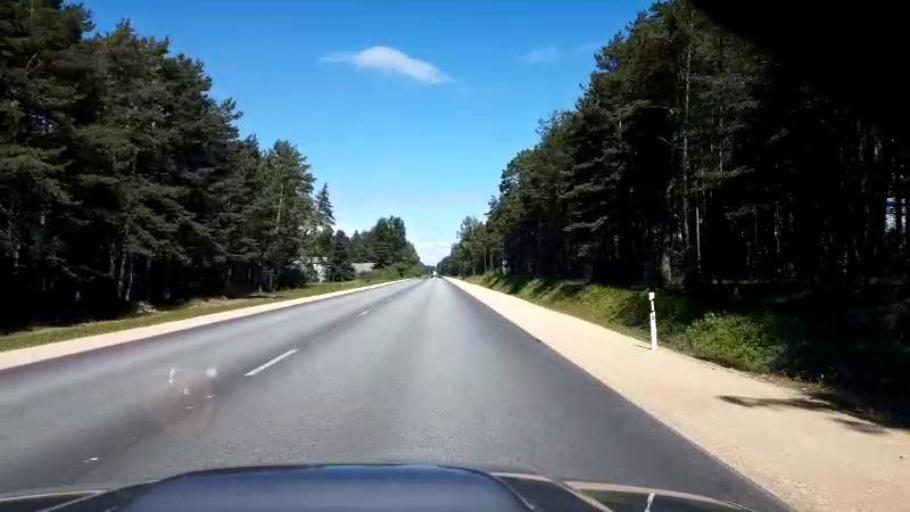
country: LV
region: Salacgrivas
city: Salacgriva
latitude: 57.7996
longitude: 24.3499
